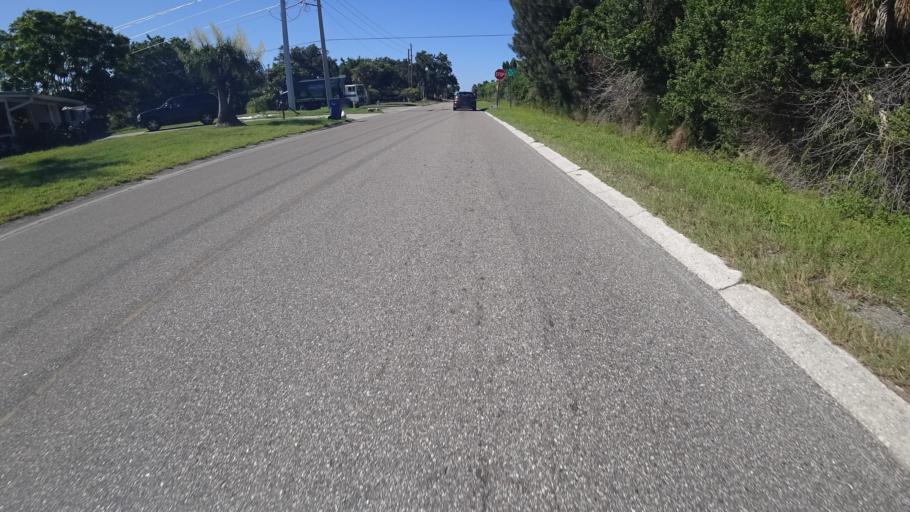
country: US
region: Florida
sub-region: Manatee County
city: Bayshore Gardens
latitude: 27.4257
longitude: -82.5960
